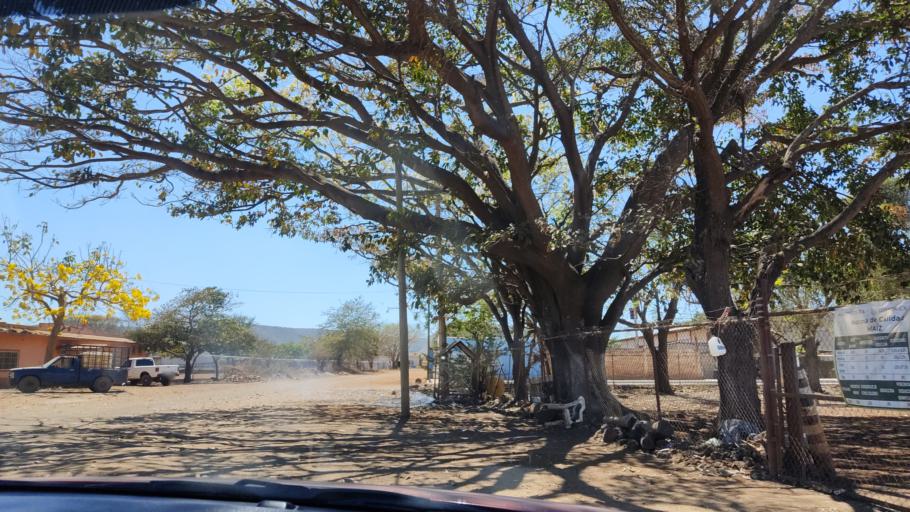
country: MX
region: Nayarit
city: Santa Maria del Oro
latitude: 21.4225
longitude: -104.6111
